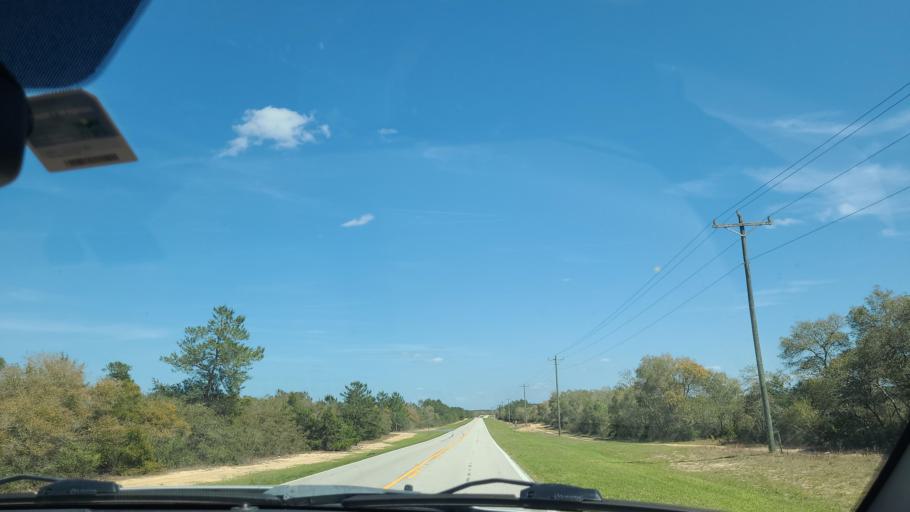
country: US
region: Florida
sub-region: Putnam County
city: Interlachen
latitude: 29.3683
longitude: -81.8522
